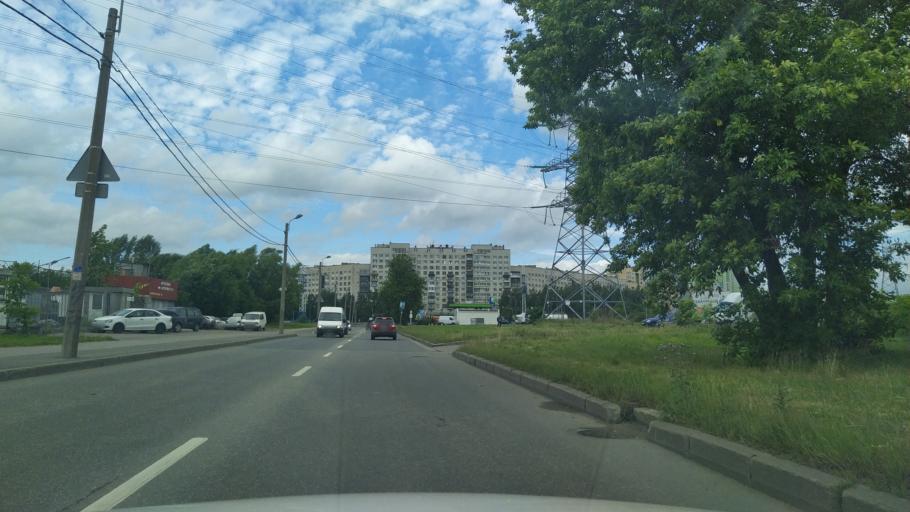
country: RU
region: Leningrad
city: Finlyandskiy
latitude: 59.9771
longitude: 30.3829
